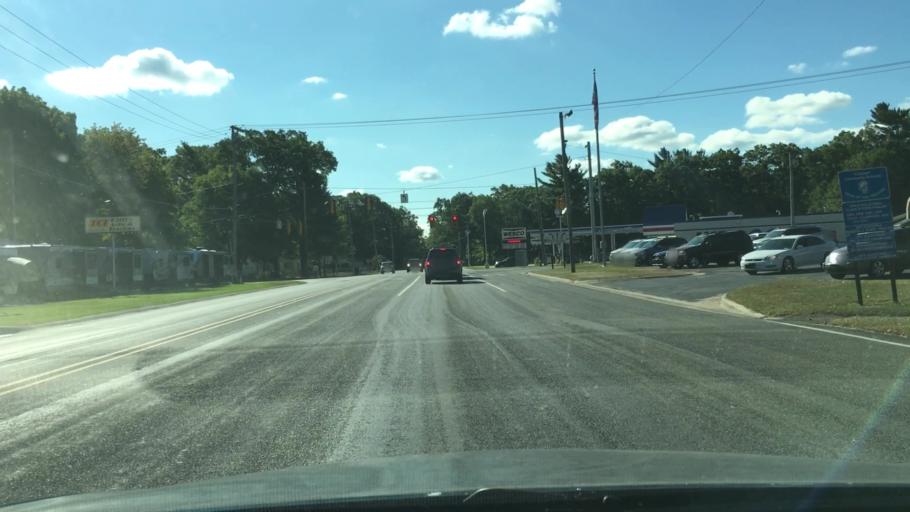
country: US
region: Michigan
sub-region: Muskegon County
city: Muskegon Heights
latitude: 43.2022
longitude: -86.1879
